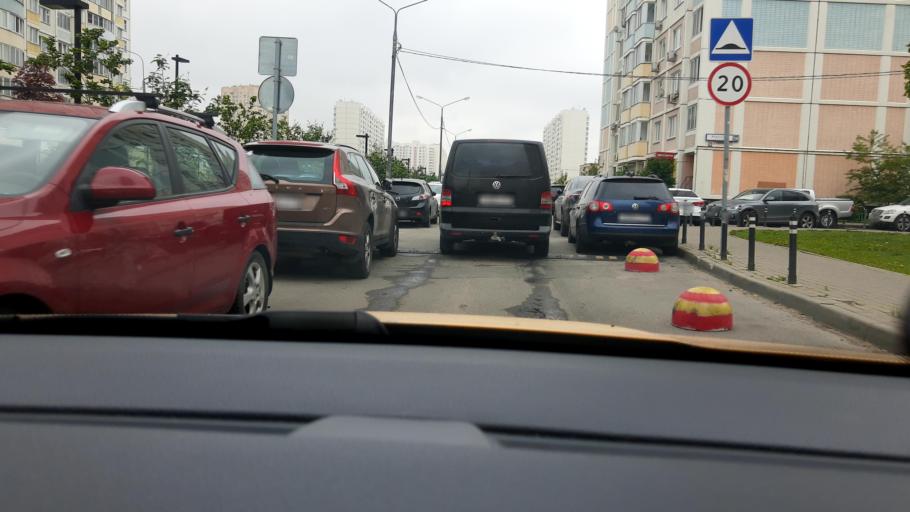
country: RU
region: Moskovskaya
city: Mytishchi
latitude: 55.9144
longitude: 37.7128
